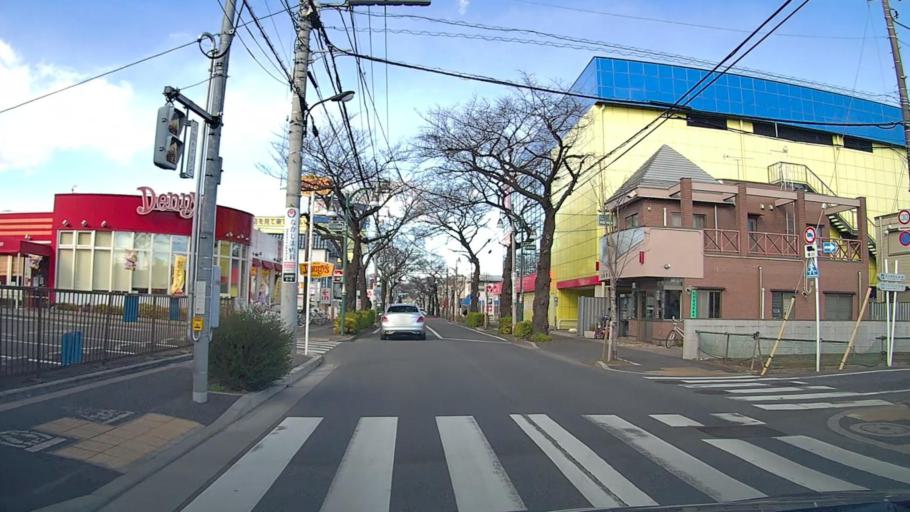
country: JP
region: Saitama
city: Asaka
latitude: 35.7677
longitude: 139.5873
